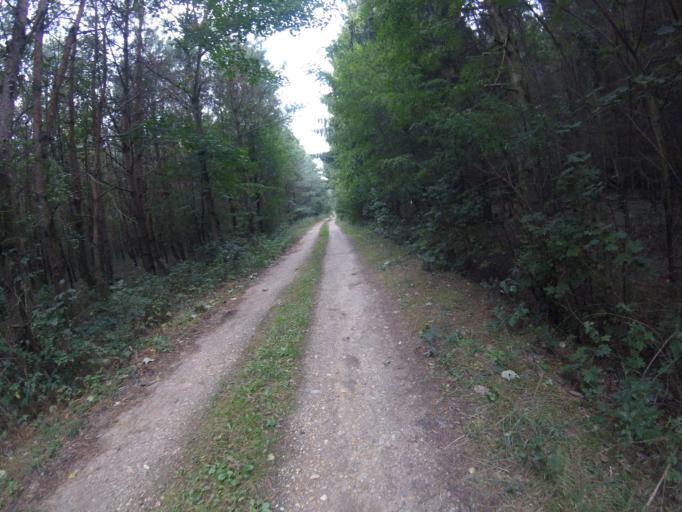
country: HU
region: Vas
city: Buk
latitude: 47.3441
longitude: 16.7592
